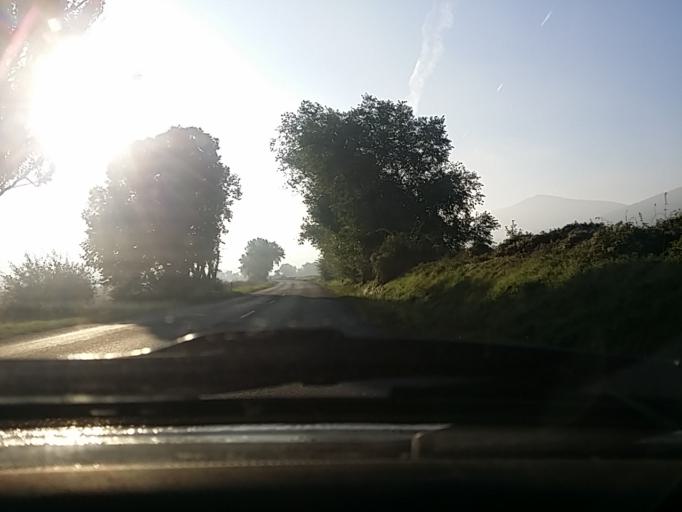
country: HU
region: Komarom-Esztergom
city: Pilismarot
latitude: 47.7780
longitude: 18.8914
